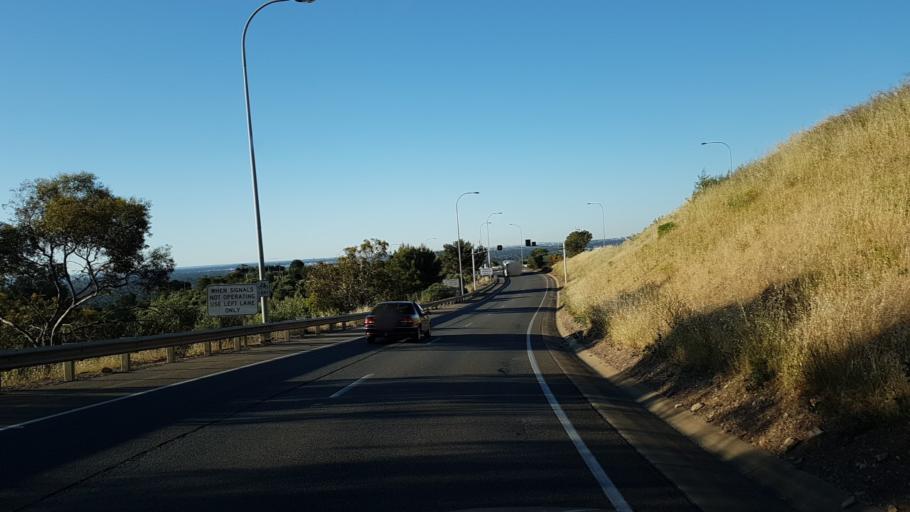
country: AU
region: South Australia
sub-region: Onkaparinga
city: Bedford Park
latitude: -35.0355
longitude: 138.5632
